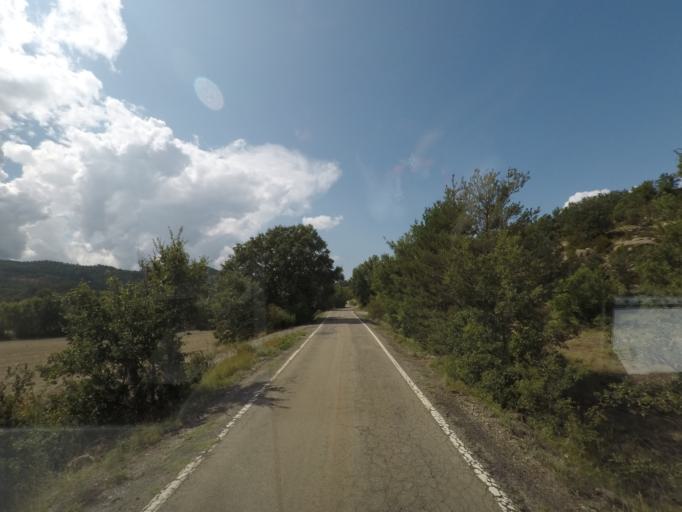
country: ES
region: Aragon
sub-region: Provincia de Huesca
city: Yebra de Basa
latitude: 42.3982
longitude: -0.3389
